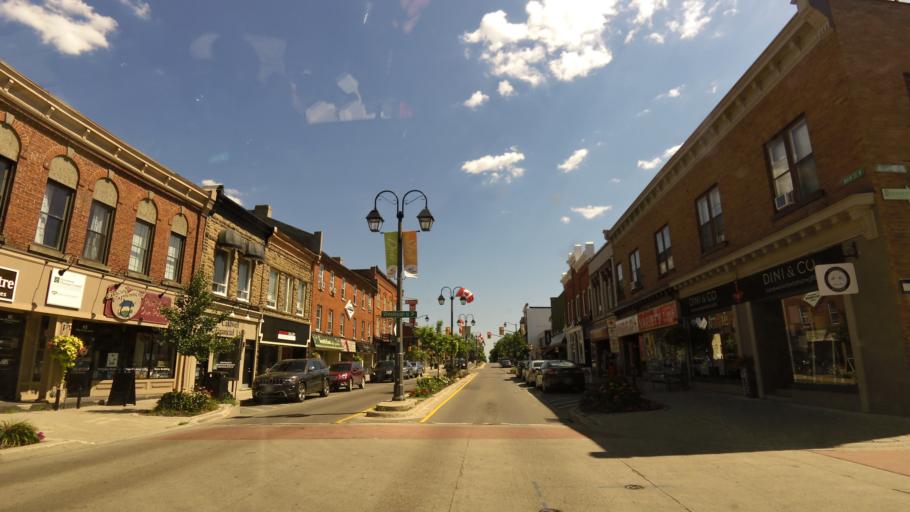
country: CA
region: Ontario
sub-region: Halton
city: Milton
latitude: 43.6499
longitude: -79.9268
